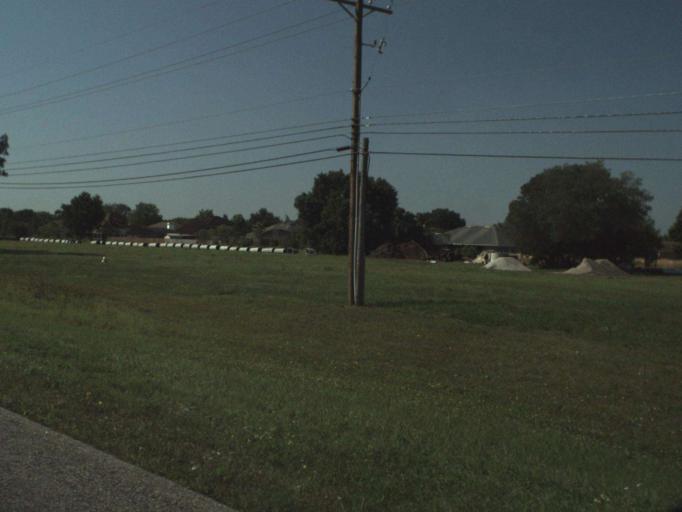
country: US
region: Florida
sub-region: Orange County
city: Wedgefield
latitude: 28.5163
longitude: -81.0645
